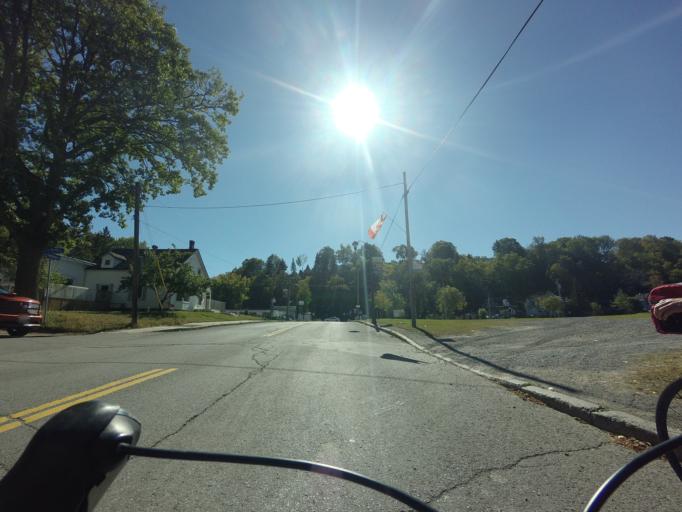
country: CA
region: Ontario
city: Clarence-Rockland
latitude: 45.5174
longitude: -75.4109
